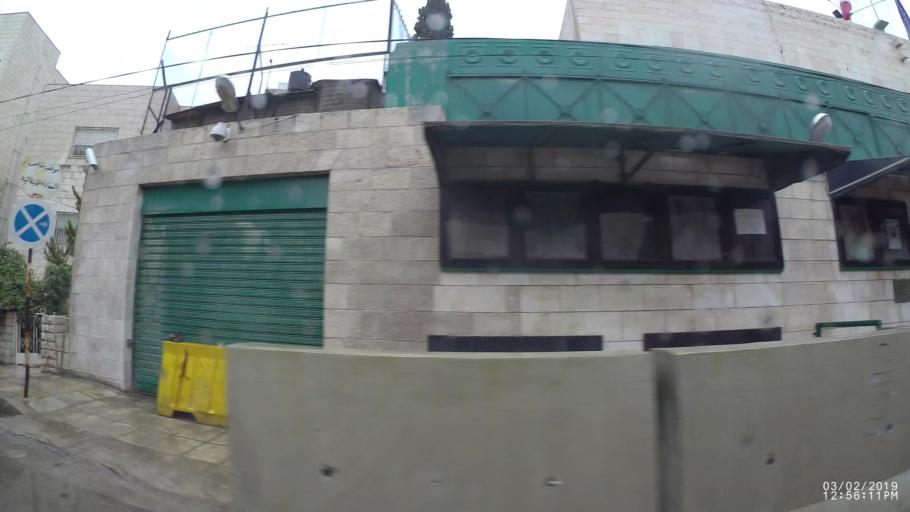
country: JO
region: Amman
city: Amman
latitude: 31.9543
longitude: 35.9267
